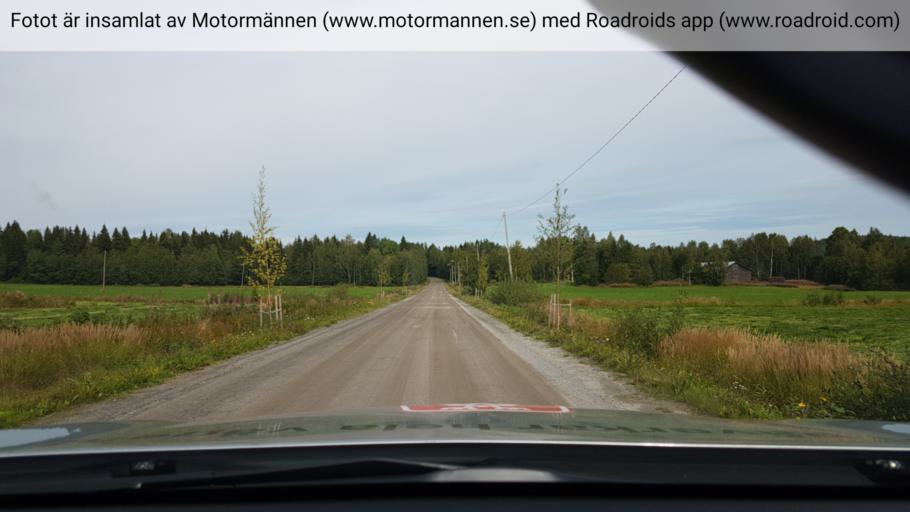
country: SE
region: Vaesterbotten
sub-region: Vannas Kommun
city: Vaennaes
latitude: 63.8308
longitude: 19.6297
